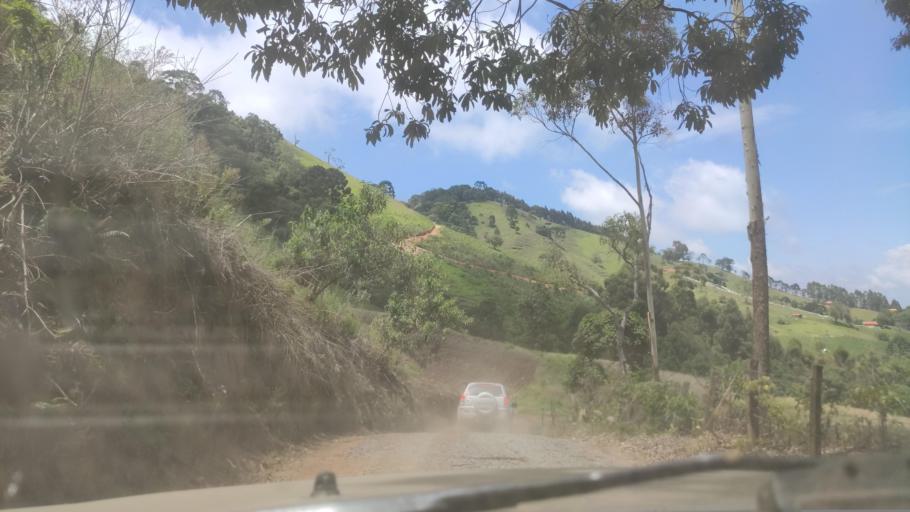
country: BR
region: Minas Gerais
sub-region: Cambui
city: Cambui
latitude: -22.6683
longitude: -45.9495
